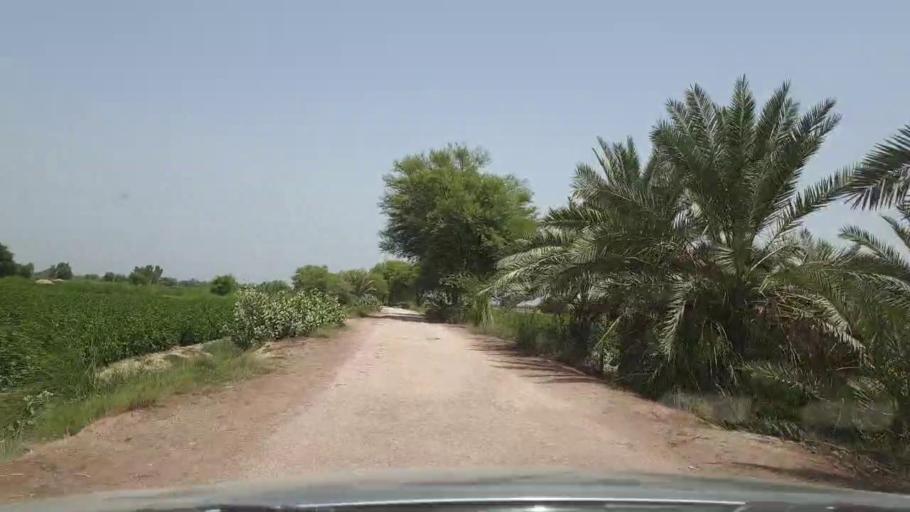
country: PK
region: Sindh
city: Pano Aqil
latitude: 27.8311
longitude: 69.1951
